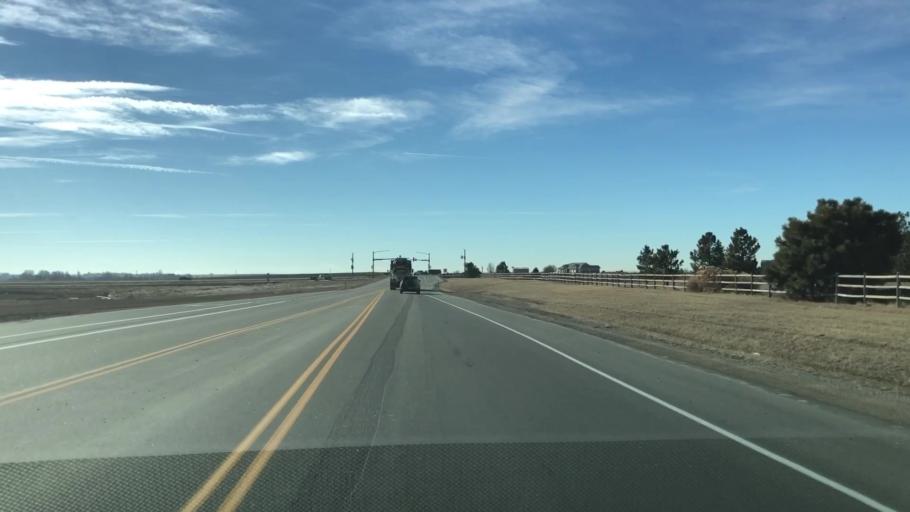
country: US
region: Colorado
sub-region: Weld County
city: Windsor
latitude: 40.4387
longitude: -104.9445
